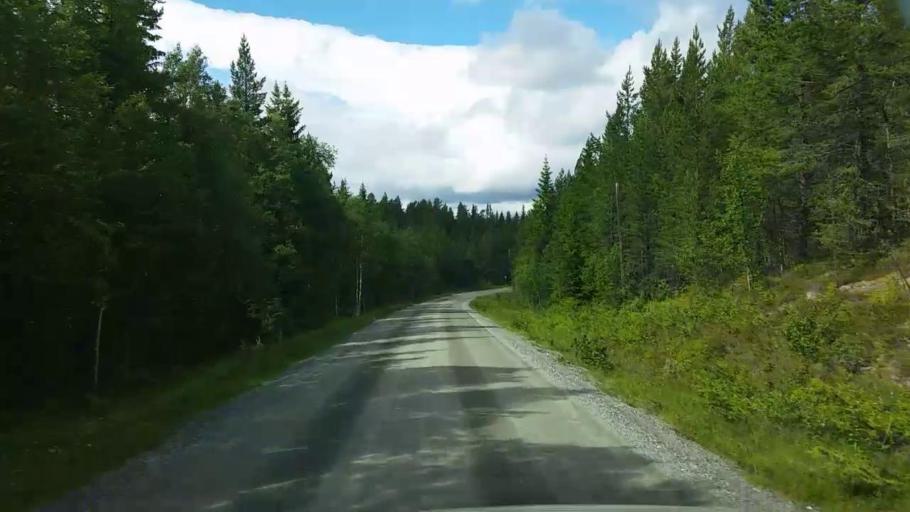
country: NO
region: Hedmark
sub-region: Engerdal
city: Engerdal
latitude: 62.4194
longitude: 12.6765
